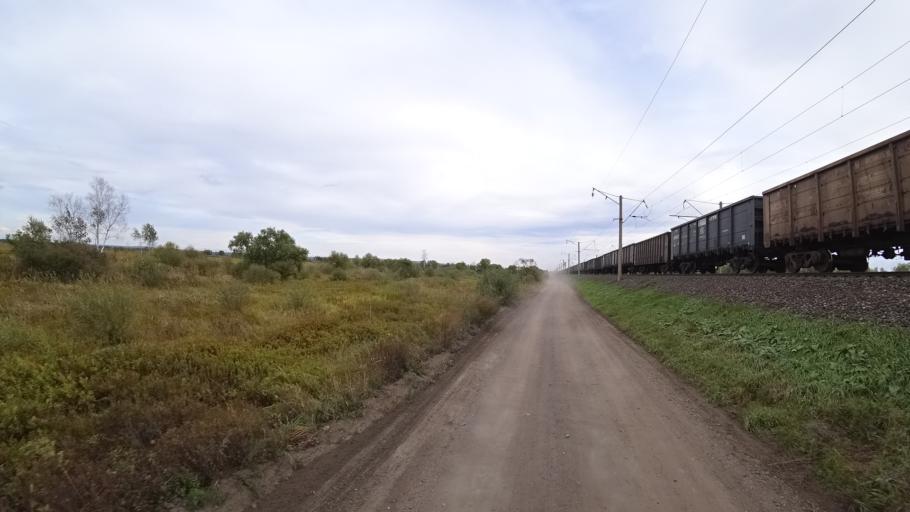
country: RU
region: Amur
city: Arkhara
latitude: 49.3591
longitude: 130.1510
